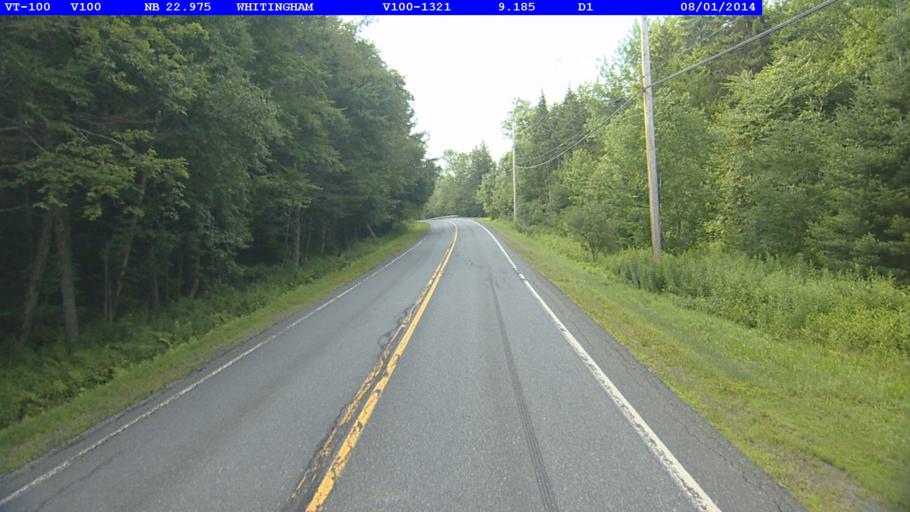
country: US
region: Vermont
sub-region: Windham County
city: Dover
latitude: 42.8114
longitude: -72.8426
